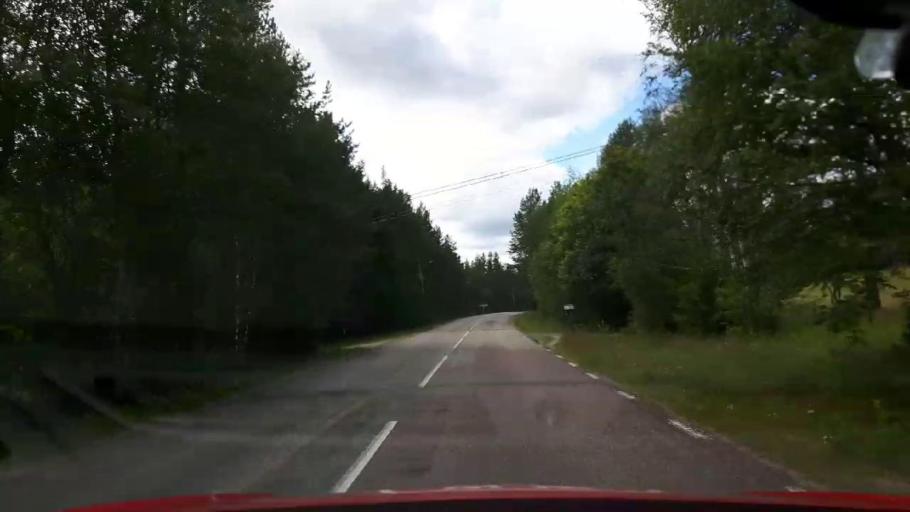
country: SE
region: Jaemtland
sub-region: Harjedalens Kommun
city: Sveg
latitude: 61.8447
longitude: 14.0462
